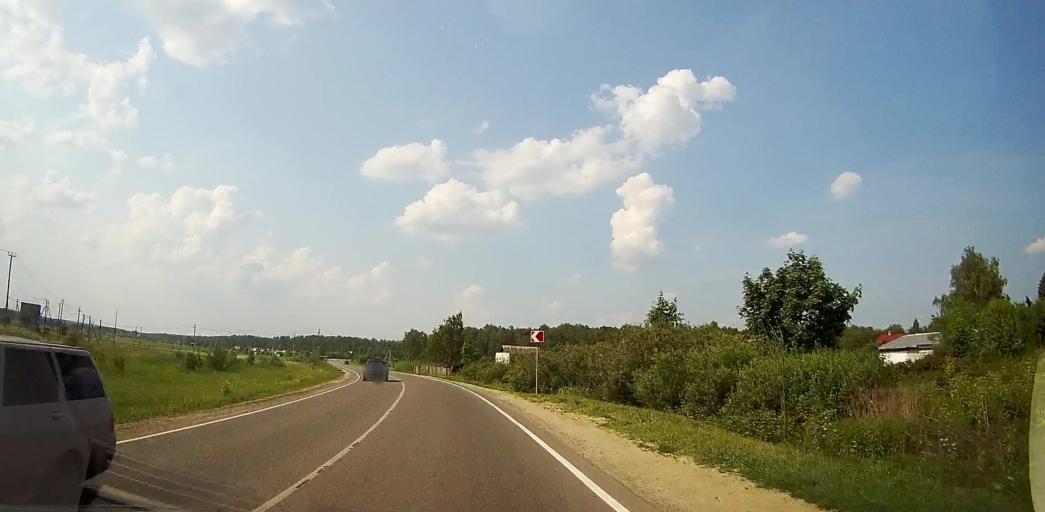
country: RU
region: Moskovskaya
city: Mikhnevo
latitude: 55.1602
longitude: 37.9619
